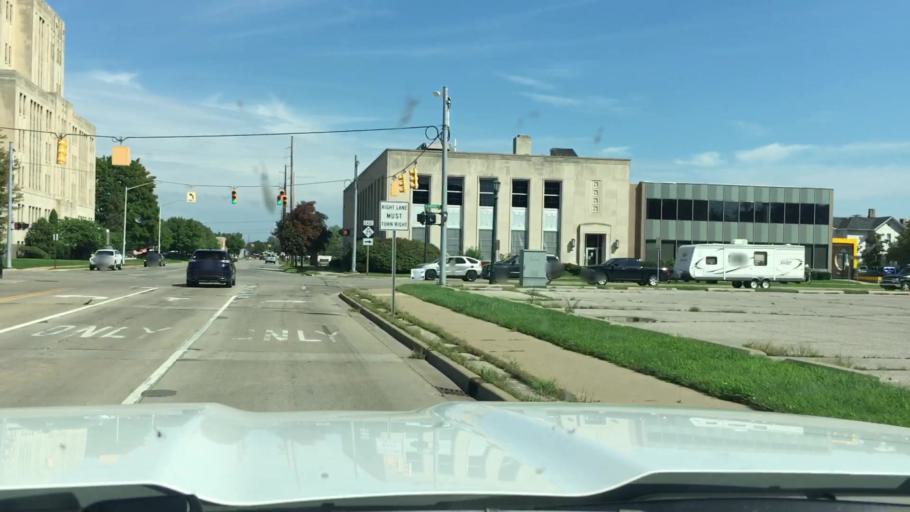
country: US
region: Michigan
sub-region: Bay County
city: Bay City
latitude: 43.5972
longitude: -83.8846
